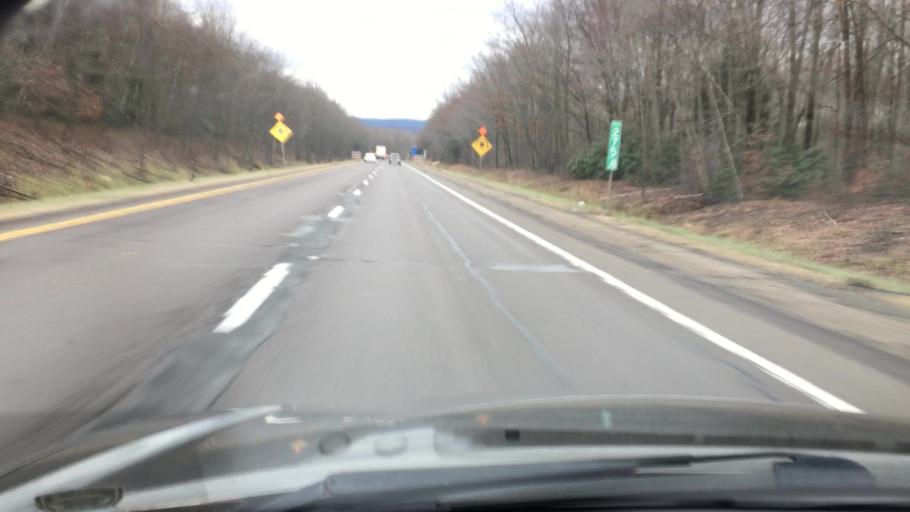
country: US
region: Pennsylvania
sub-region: Luzerne County
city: White Haven
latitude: 41.0596
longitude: -75.7168
